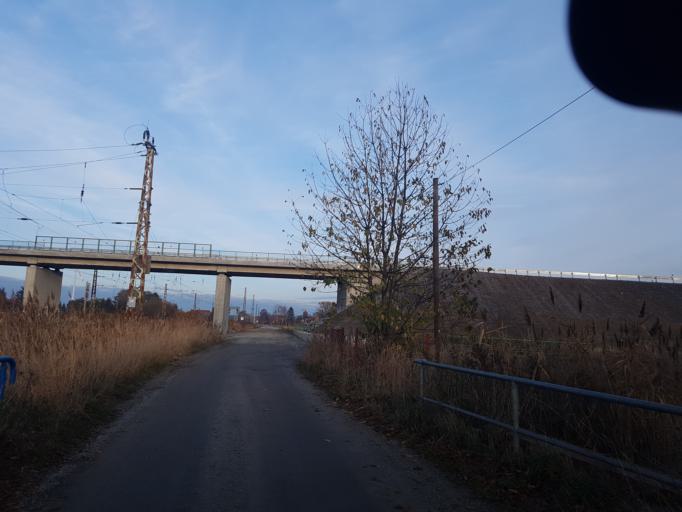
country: DE
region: Brandenburg
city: Finsterwalde
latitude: 51.6420
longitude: 13.7226
